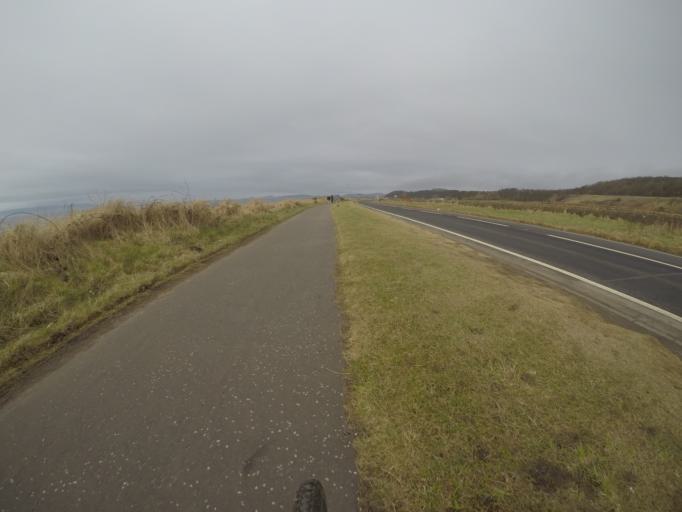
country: GB
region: Scotland
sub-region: North Ayrshire
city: Ardrossan
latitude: 55.6563
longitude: -4.8273
